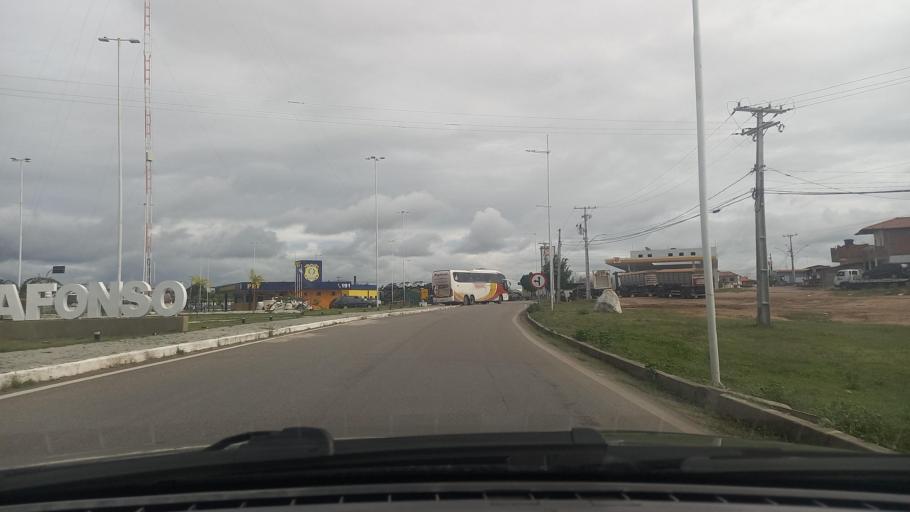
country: BR
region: Bahia
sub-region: Paulo Afonso
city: Paulo Afonso
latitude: -9.4368
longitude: -38.2038
